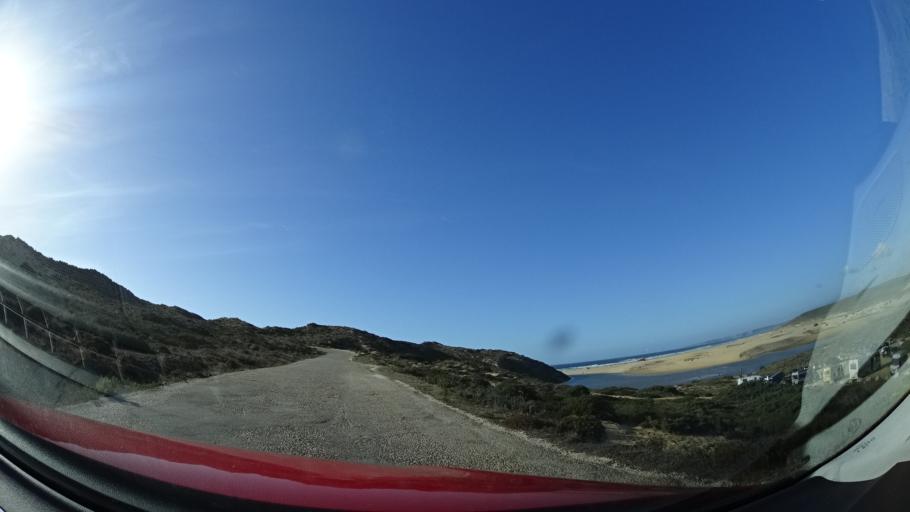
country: PT
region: Faro
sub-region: Vila do Bispo
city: Vila do Bispo
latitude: 37.1922
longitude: -8.9032
